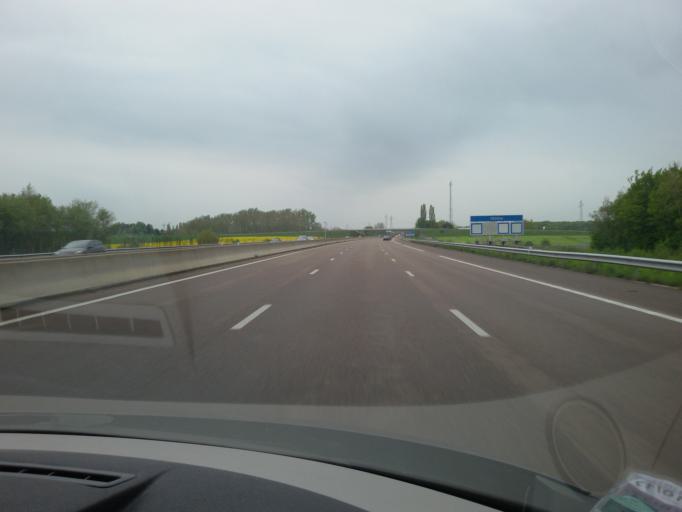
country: FR
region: Bourgogne
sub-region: Departement de la Cote-d'Or
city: Gevrey-Chambertin
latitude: 47.2066
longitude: 4.9979
